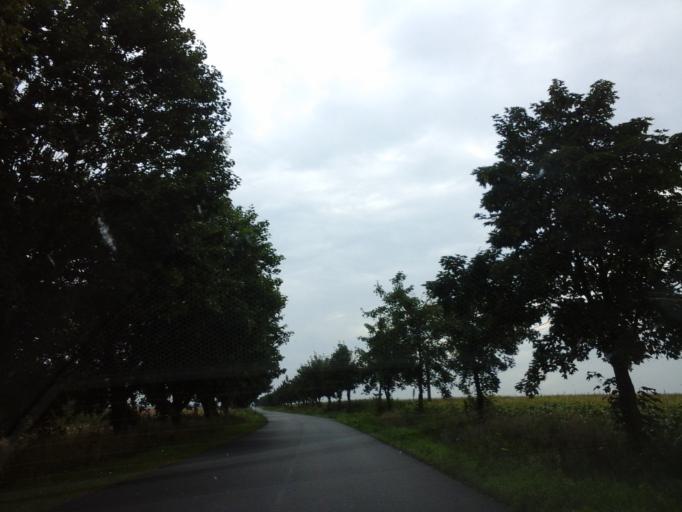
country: PL
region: Lower Silesian Voivodeship
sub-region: Powiat zabkowicki
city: Cieplowody
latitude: 50.6696
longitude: 16.9160
